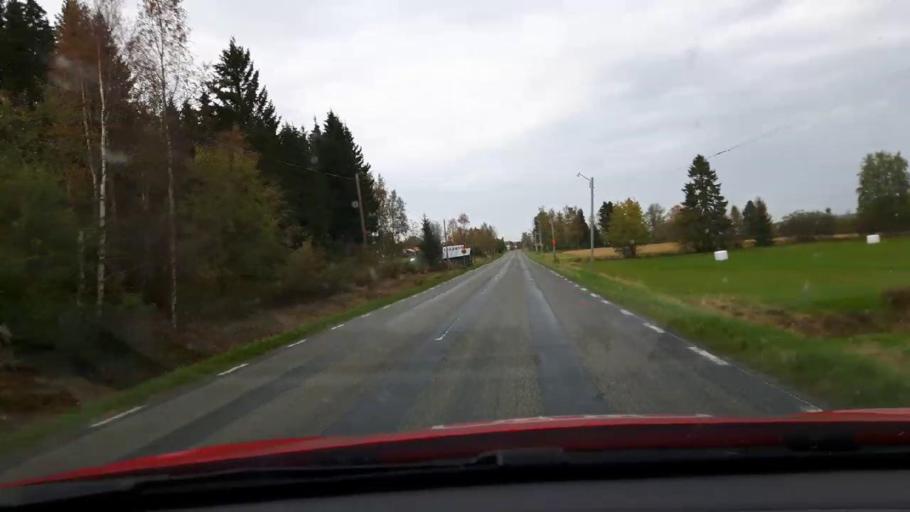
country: SE
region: Jaemtland
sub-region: Bergs Kommun
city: Hoverberg
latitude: 62.8281
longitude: 14.3894
